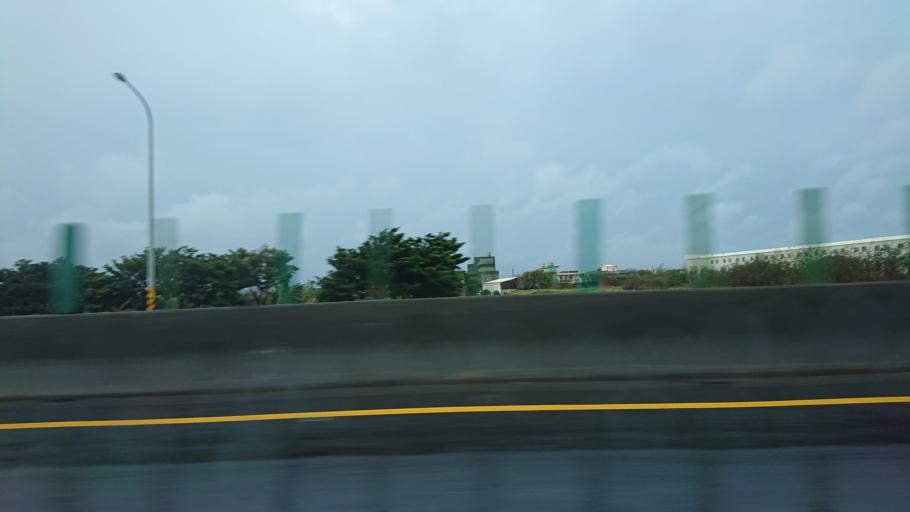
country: TW
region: Taiwan
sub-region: Changhua
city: Chang-hua
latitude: 24.1378
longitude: 120.4432
